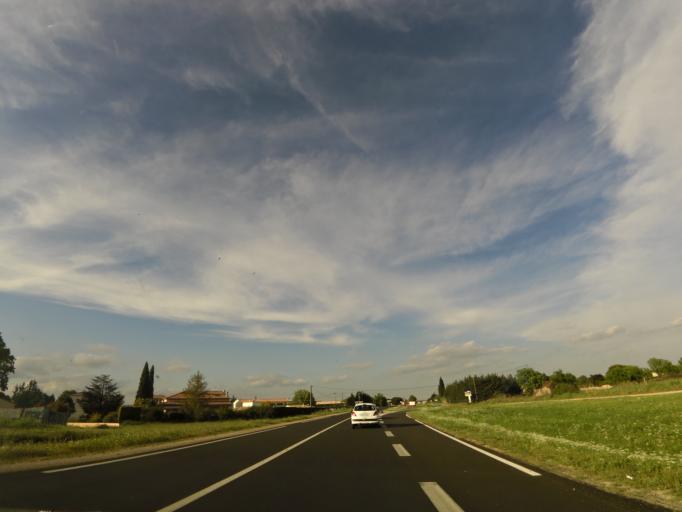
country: FR
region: Languedoc-Roussillon
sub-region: Departement de l'Herault
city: Lunel
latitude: 43.6659
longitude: 4.1404
